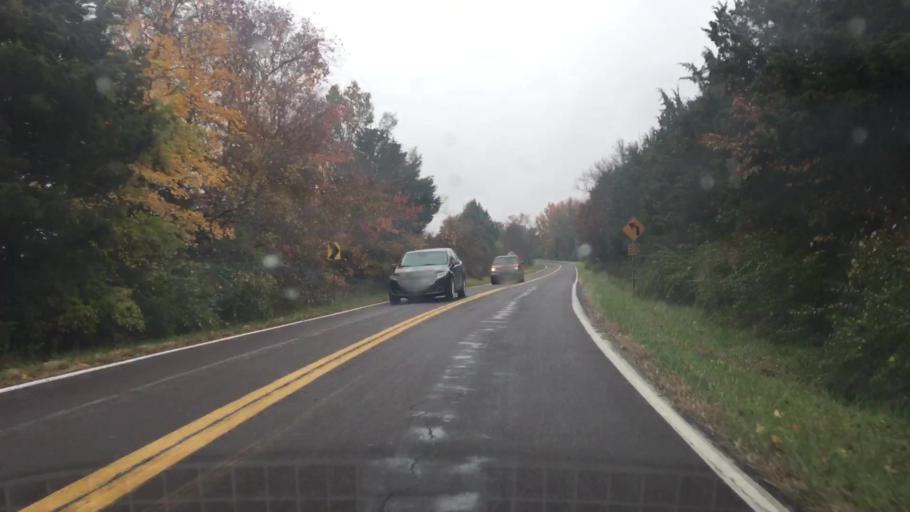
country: US
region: Missouri
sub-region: Callaway County
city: Fulton
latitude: 38.8379
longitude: -91.9204
